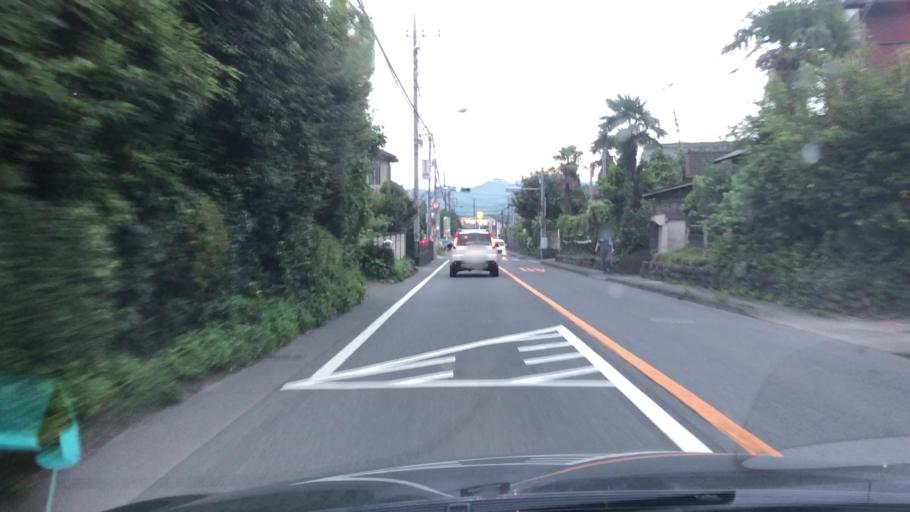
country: JP
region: Tokyo
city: Ome
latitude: 35.7925
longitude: 139.2177
